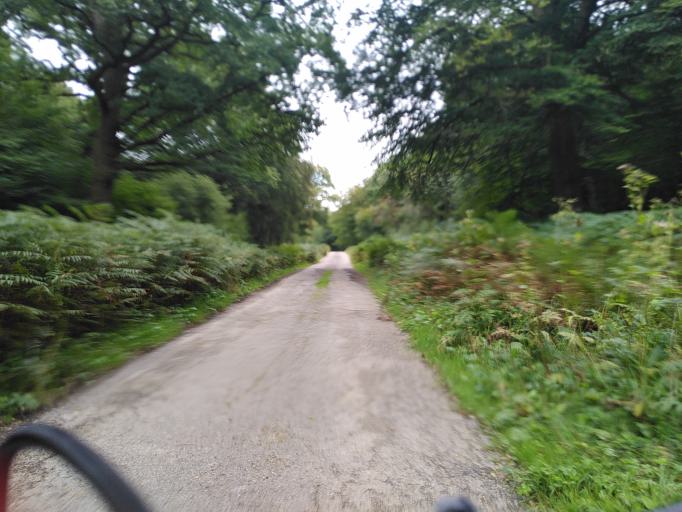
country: FR
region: Nord-Pas-de-Calais
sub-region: Departement du Pas-de-Calais
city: Desvres
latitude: 50.6872
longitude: 1.8225
